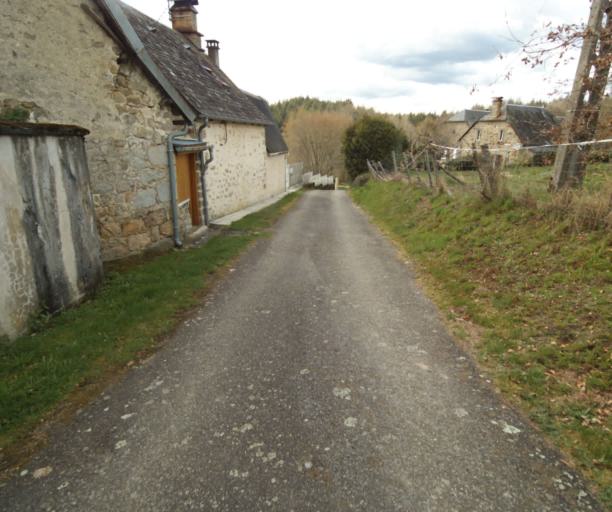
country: FR
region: Limousin
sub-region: Departement de la Correze
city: Argentat
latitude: 45.2136
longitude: 1.9587
